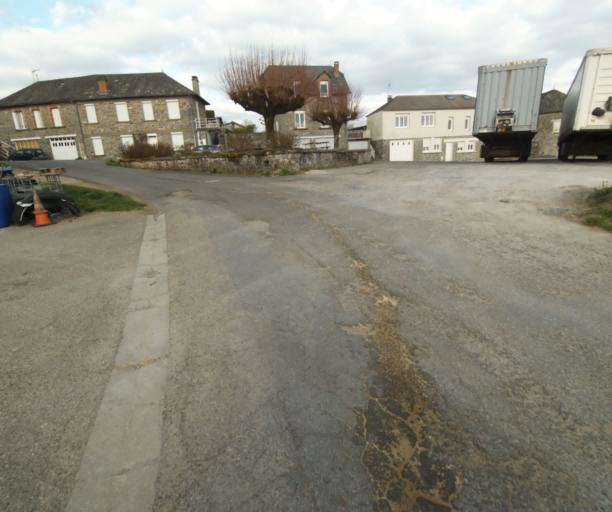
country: FR
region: Limousin
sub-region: Departement de la Correze
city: Saint-Clement
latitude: 45.3563
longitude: 1.6388
